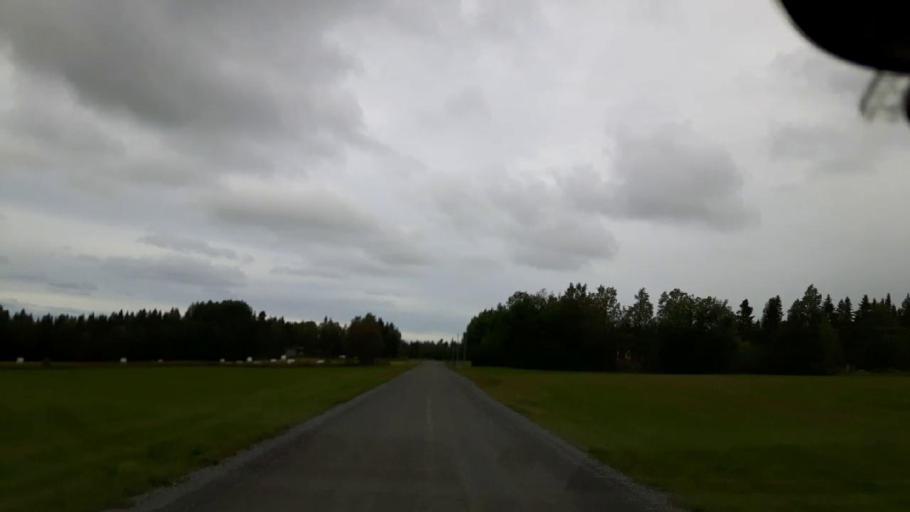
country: SE
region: Jaemtland
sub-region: OEstersunds Kommun
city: Ostersund
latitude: 63.0908
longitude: 14.5549
